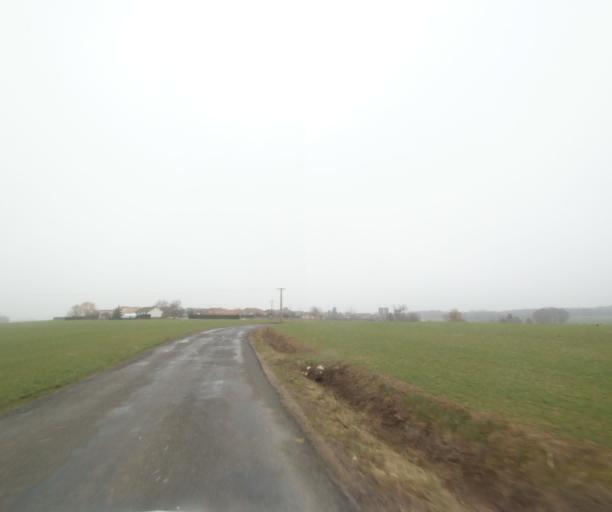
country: FR
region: Champagne-Ardenne
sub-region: Departement de la Haute-Marne
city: Bienville
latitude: 48.5269
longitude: 5.0432
